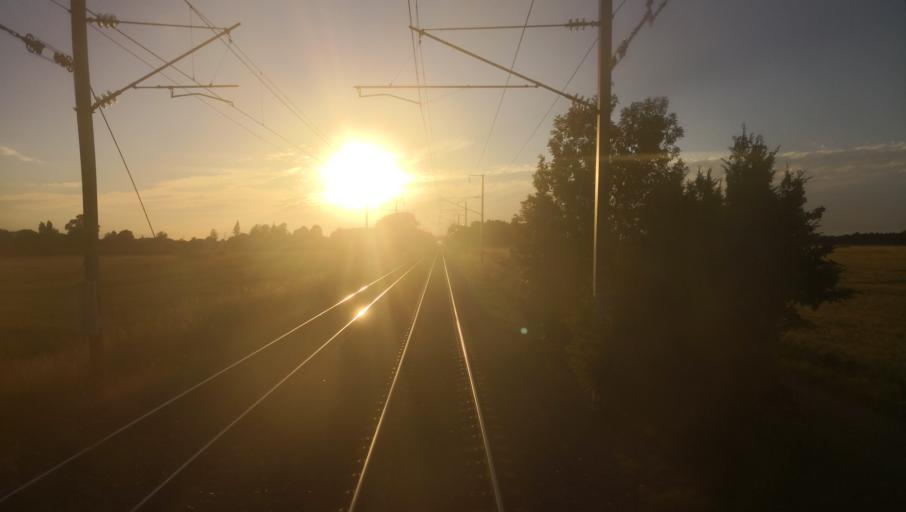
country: FR
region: Haute-Normandie
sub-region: Departement de l'Eure
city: Conches-en-Ouche
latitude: 48.9973
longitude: 0.8687
